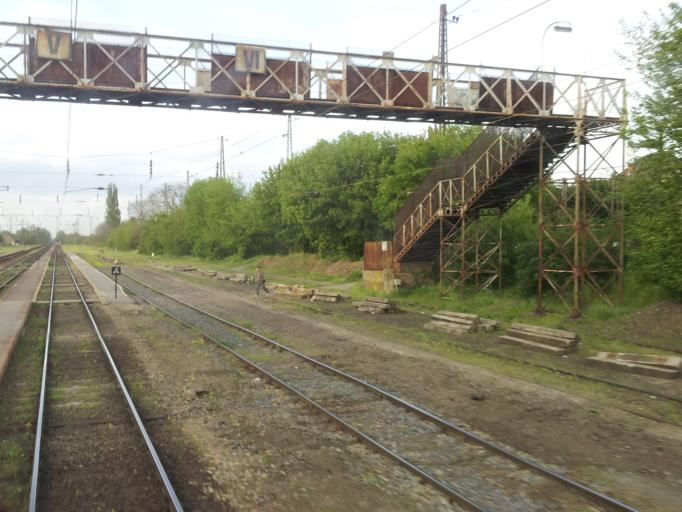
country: HU
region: Budapest
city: Budapest XV. keruelet
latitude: 47.5651
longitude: 19.1123
